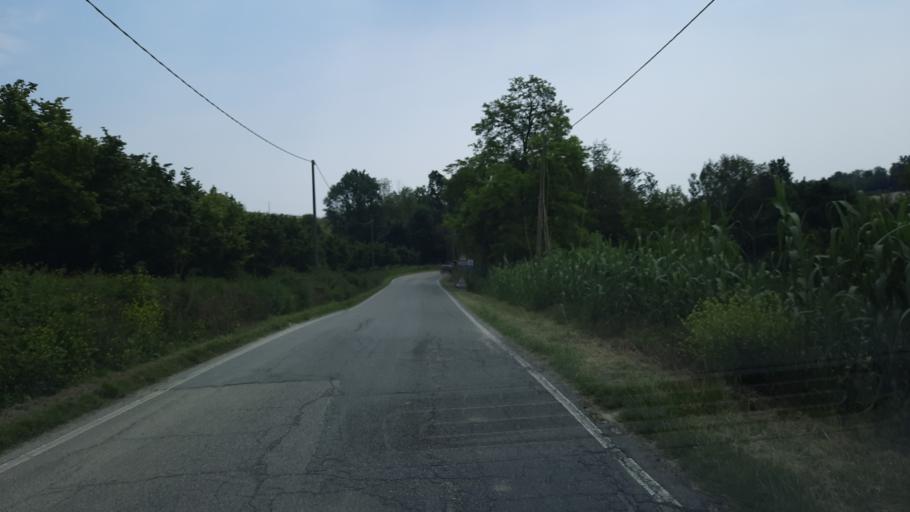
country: IT
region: Piedmont
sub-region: Provincia di Alessandria
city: Ozzano Monferrato
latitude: 45.1004
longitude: 8.3845
